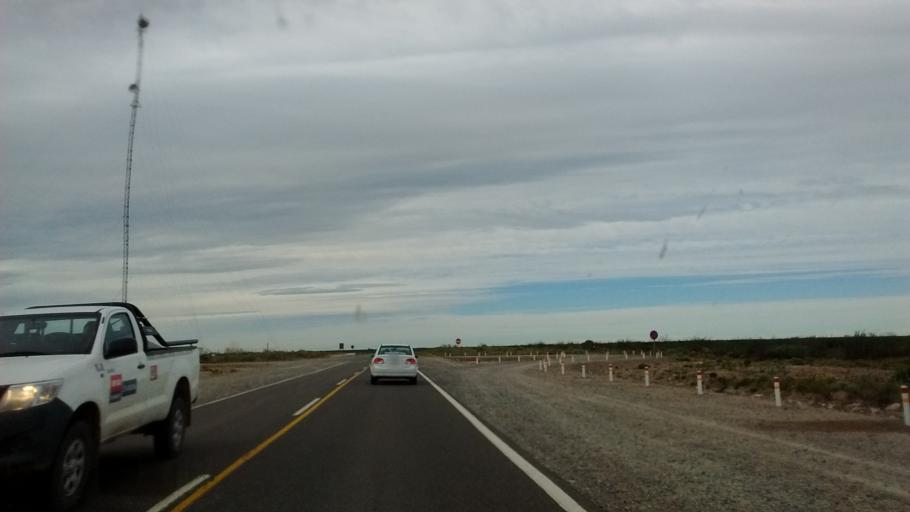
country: AR
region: Rio Negro
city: Contraalmirante Cordero
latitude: -38.3241
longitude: -68.0068
